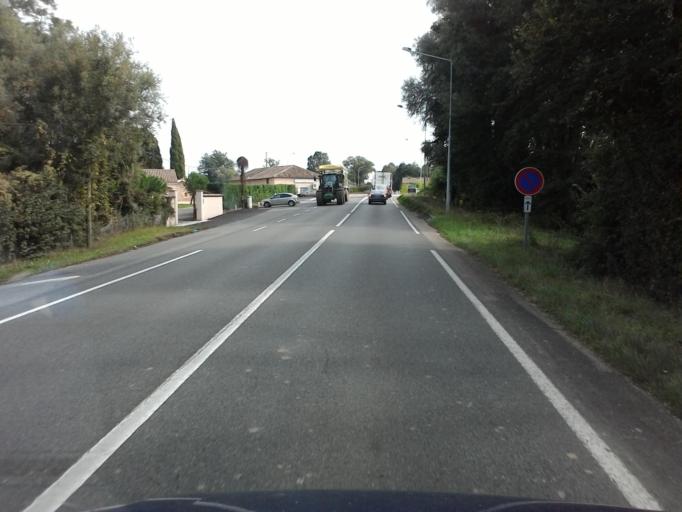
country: FR
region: Rhone-Alpes
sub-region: Departement de l'Ain
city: Crottet
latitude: 46.2894
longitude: 4.9105
